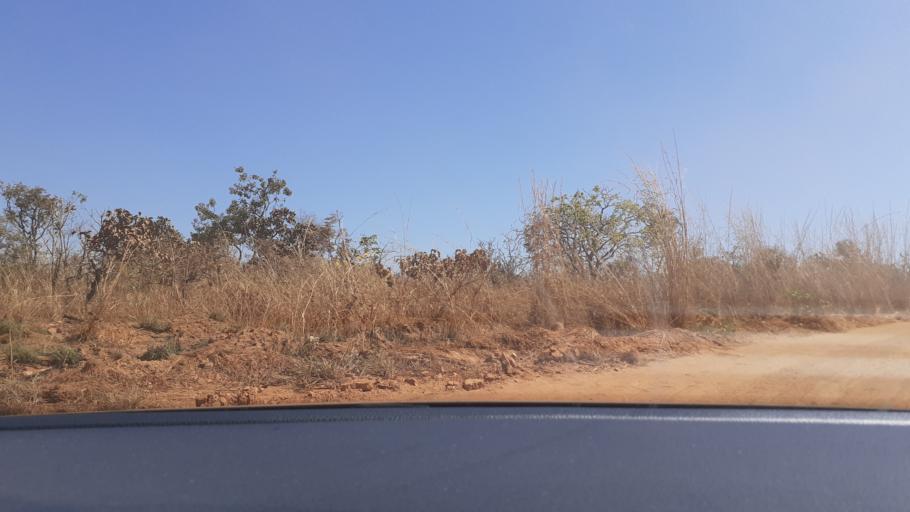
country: BR
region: Goias
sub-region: Aparecida De Goiania
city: Aparecida de Goiania
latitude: -16.8719
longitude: -49.2809
